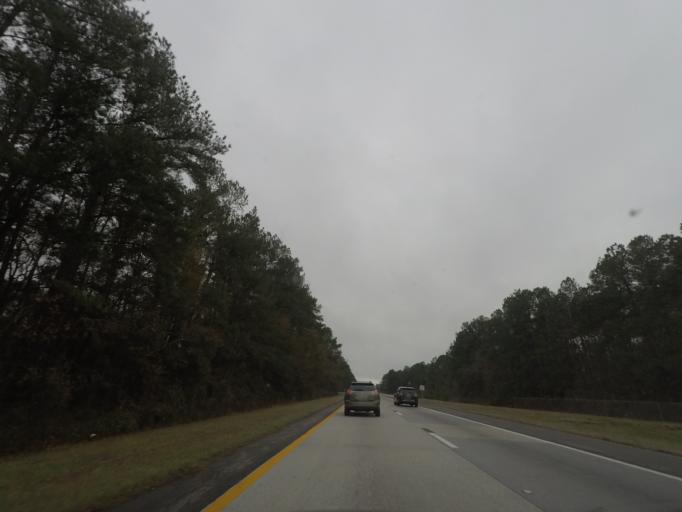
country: US
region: South Carolina
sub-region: Dorchester County
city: Saint George
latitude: 33.1580
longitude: -80.6219
